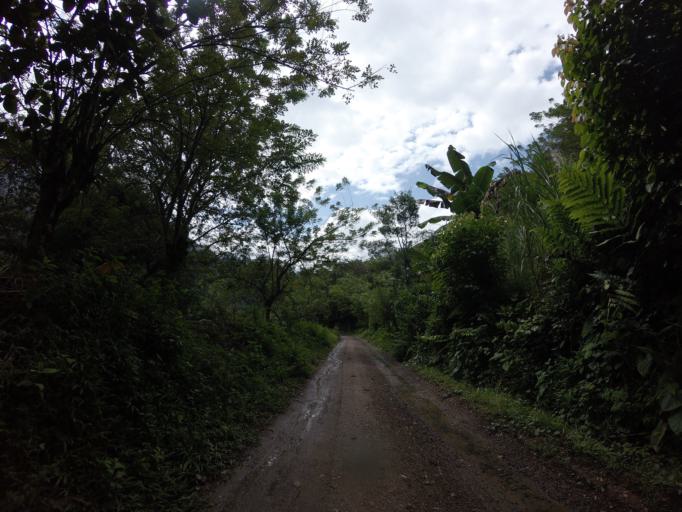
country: CO
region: Antioquia
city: Narino
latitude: 5.5357
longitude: -75.1363
